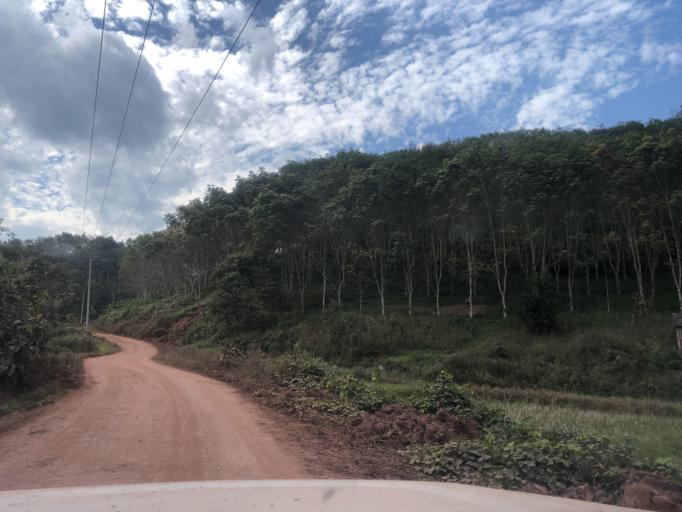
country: CN
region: Yunnan
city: Menglie
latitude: 22.1131
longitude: 101.7149
